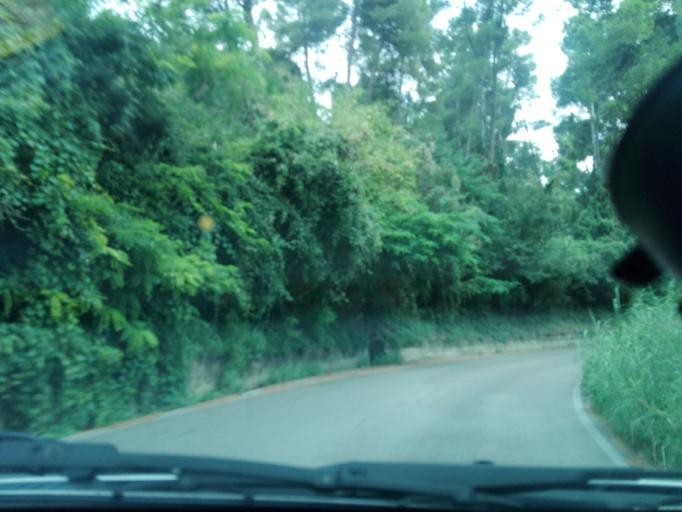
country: IT
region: Abruzzo
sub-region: Provincia di Pescara
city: Montesilvano Marina
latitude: 42.4937
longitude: 14.1451
